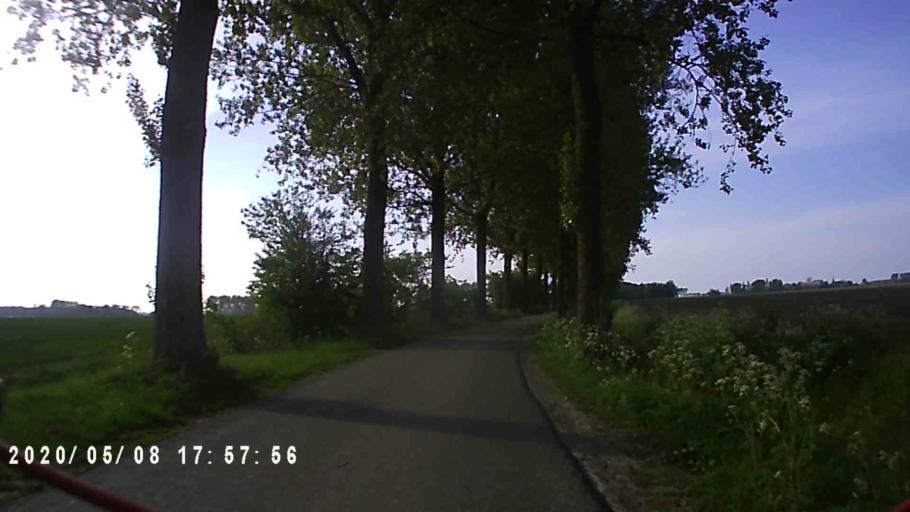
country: NL
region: Groningen
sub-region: Gemeente Winsum
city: Winsum
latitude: 53.3689
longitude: 6.4849
